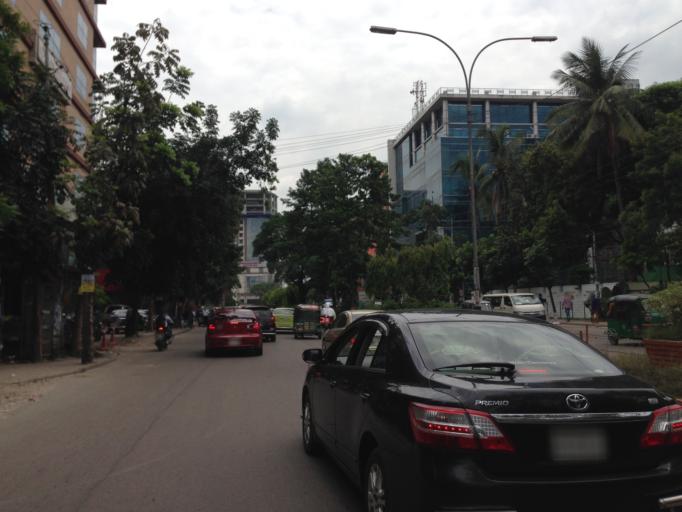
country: BD
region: Dhaka
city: Paltan
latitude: 23.7761
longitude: 90.4165
